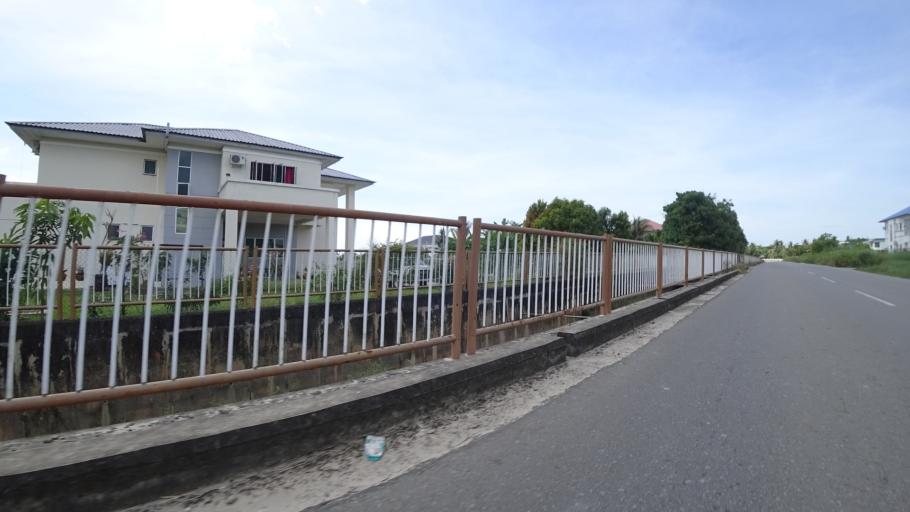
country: BN
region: Brunei and Muara
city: Bandar Seri Begawan
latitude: 4.8865
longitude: 114.8529
